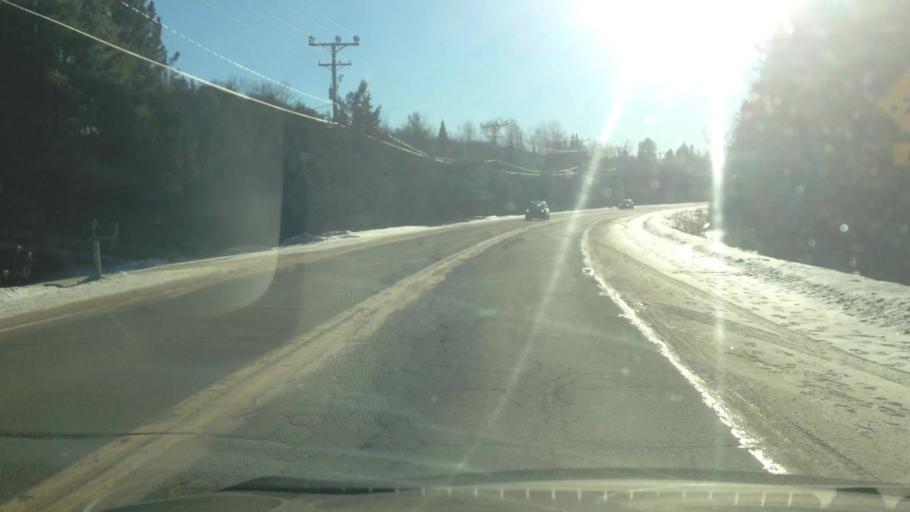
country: CA
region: Quebec
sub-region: Laurentides
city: Mont-Tremblant
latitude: 46.0908
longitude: -74.6074
